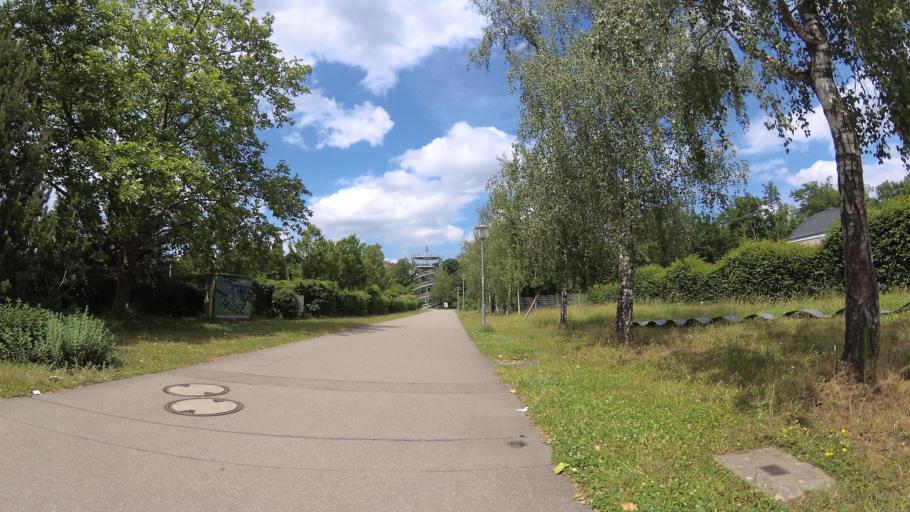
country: DE
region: Baden-Wuerttemberg
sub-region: Freiburg Region
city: Weil am Rhein
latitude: 47.5870
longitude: 7.6163
